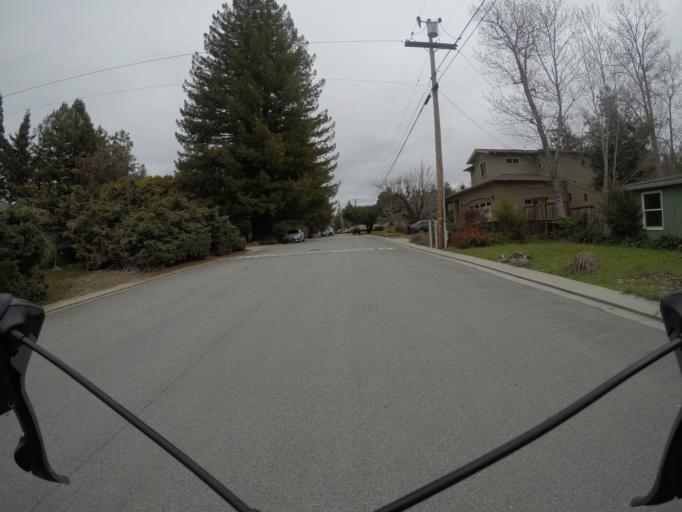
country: US
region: California
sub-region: Santa Cruz County
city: Scotts Valley
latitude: 37.0597
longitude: -122.0039
